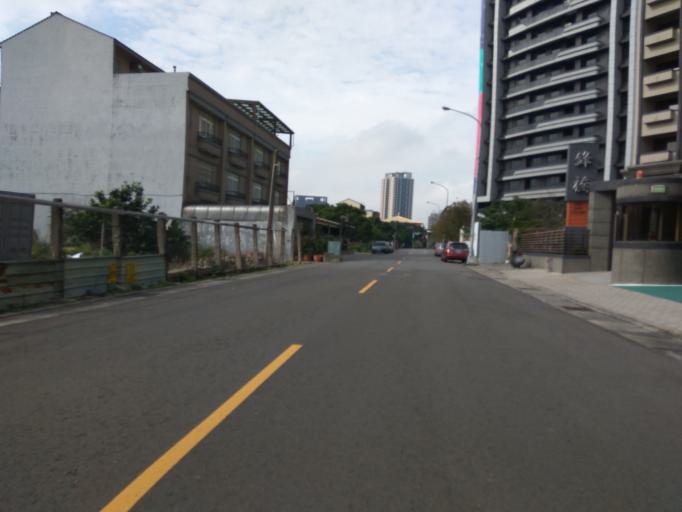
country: TW
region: Taiwan
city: Taoyuan City
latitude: 25.0049
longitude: 121.2177
